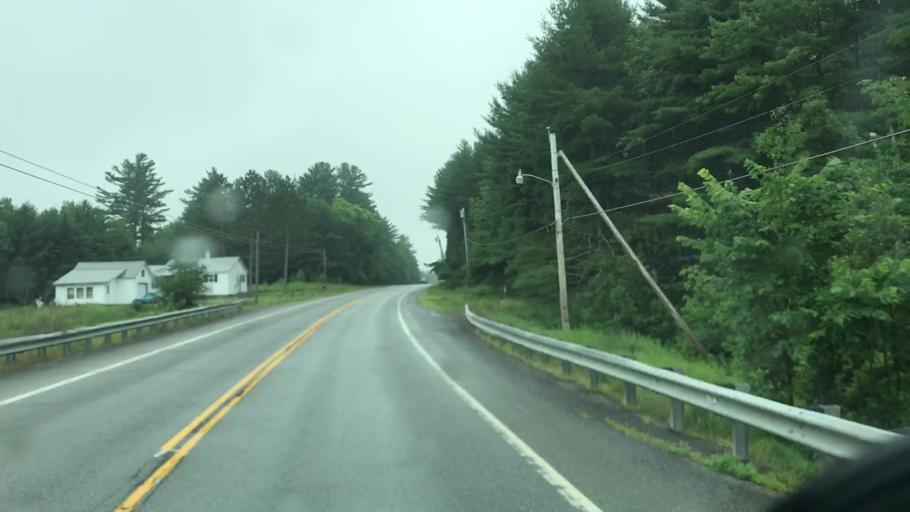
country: US
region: Maine
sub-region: Penobscot County
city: Howland
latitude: 45.2872
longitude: -68.6246
